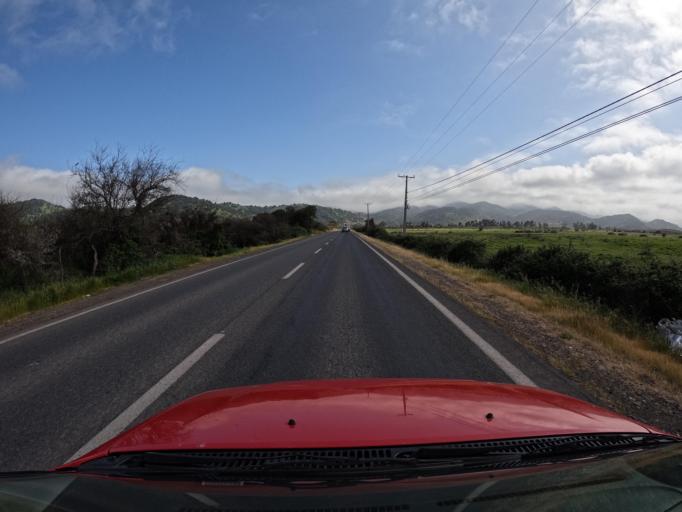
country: CL
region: Maule
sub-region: Provincia de Curico
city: Teno
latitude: -34.8367
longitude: -71.1882
